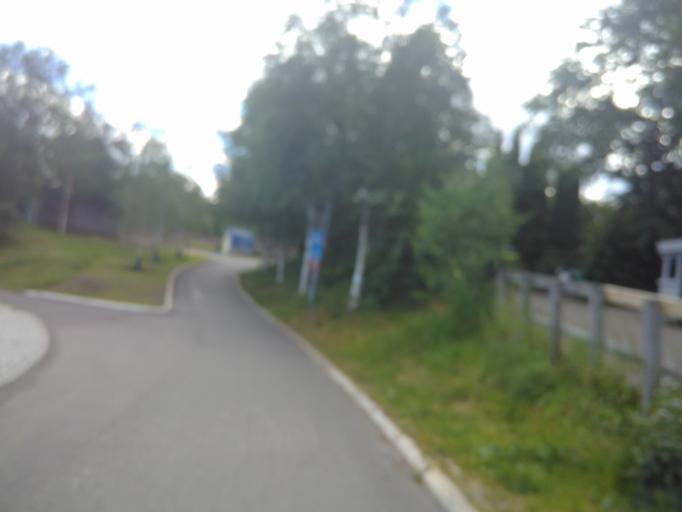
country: NO
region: Oslo
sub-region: Oslo
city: Sjolyststranda
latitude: 59.9295
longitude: 10.6594
